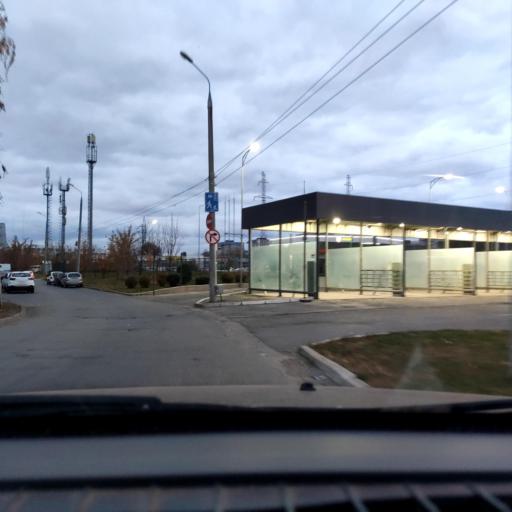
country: RU
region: Samara
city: Tol'yatti
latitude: 53.5502
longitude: 49.3206
